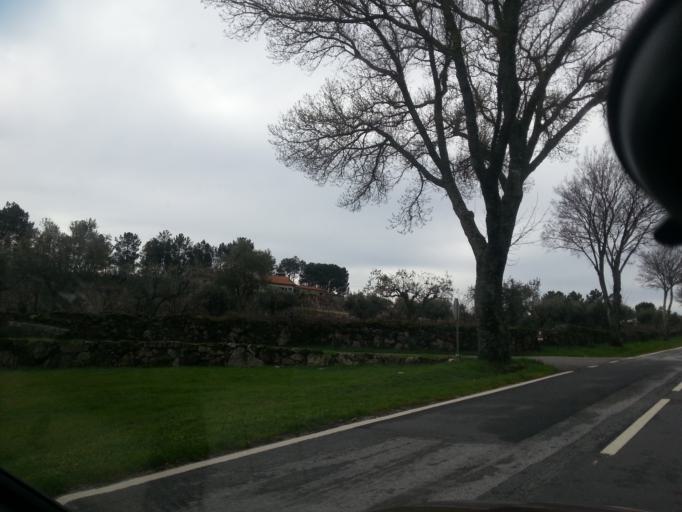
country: PT
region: Guarda
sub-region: Fornos de Algodres
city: Fornos de Algodres
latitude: 40.5280
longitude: -7.5884
